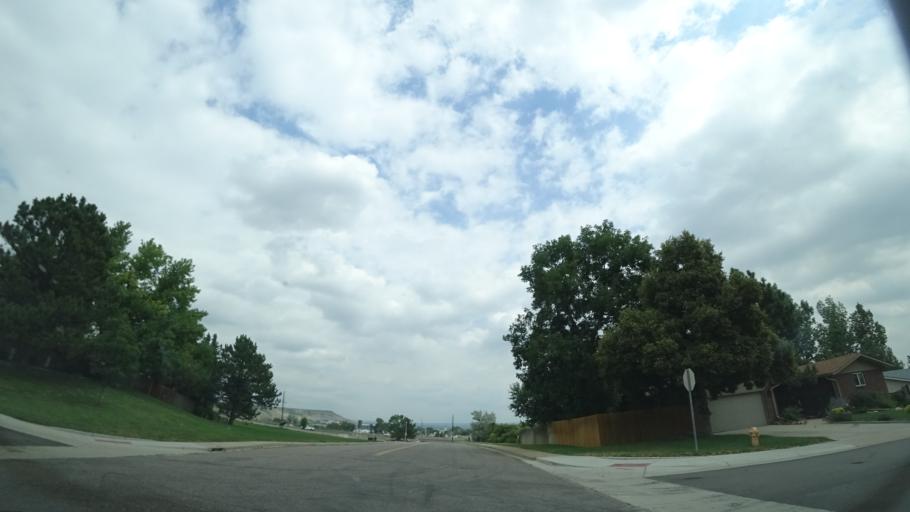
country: US
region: Colorado
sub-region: Jefferson County
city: West Pleasant View
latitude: 39.7234
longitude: -105.1596
